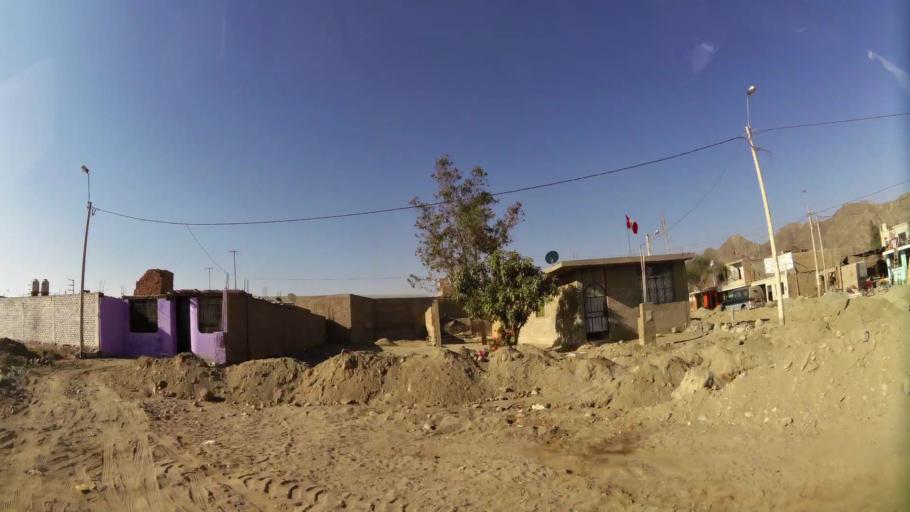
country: PE
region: Ica
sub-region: Provincia de Ica
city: La Tinguina
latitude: -14.0461
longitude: -75.6961
